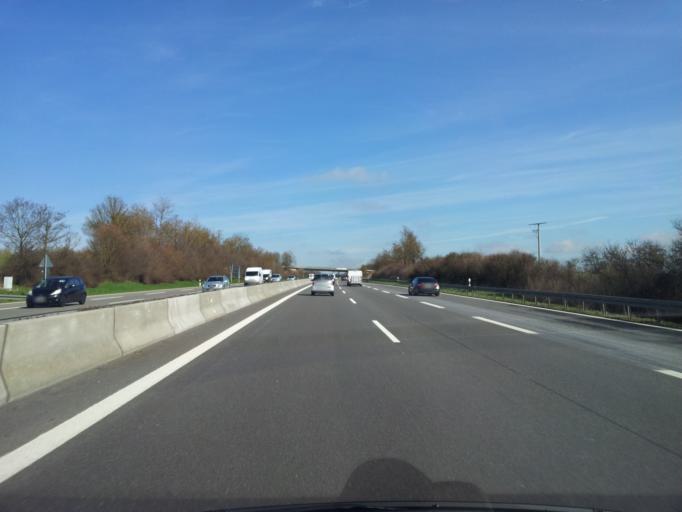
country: DE
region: Baden-Wuerttemberg
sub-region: Freiburg Region
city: Zimmern ob Rottweil
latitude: 48.1442
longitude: 8.5708
